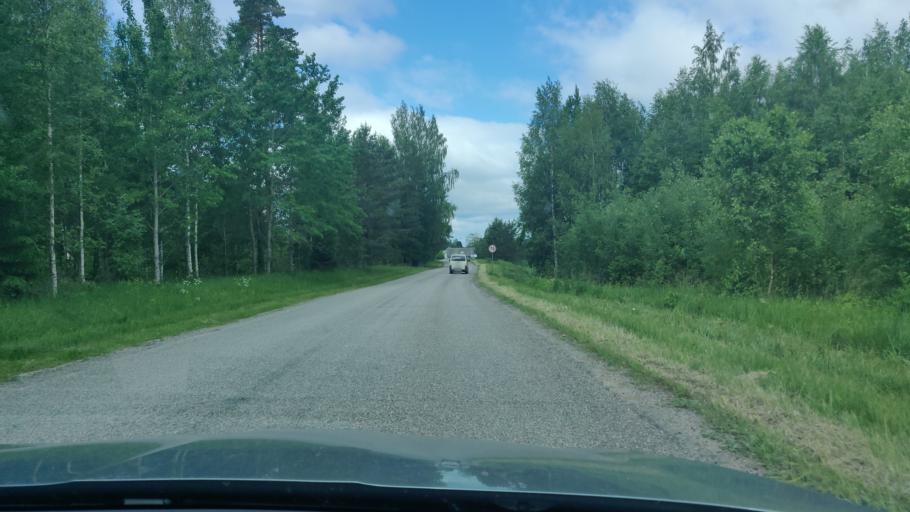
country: EE
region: Vorumaa
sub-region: Voru linn
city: Voru
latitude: 57.7277
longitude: 27.3068
